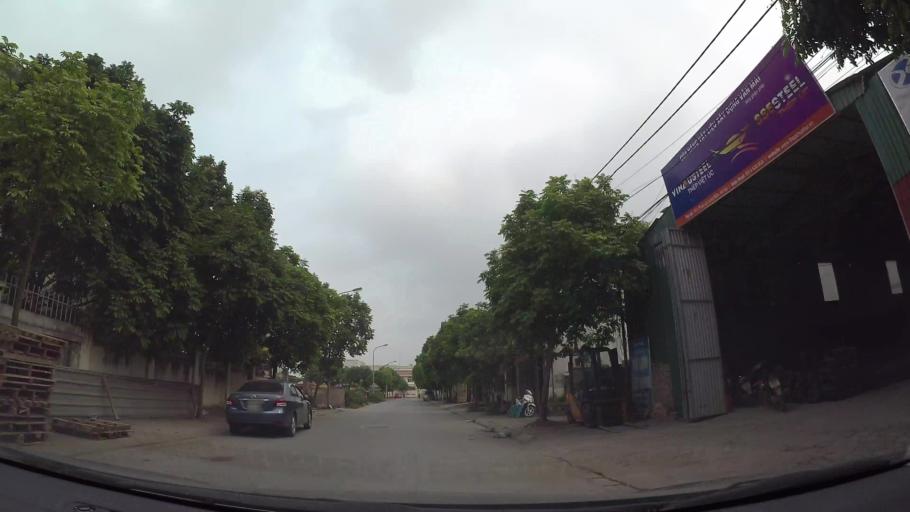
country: VN
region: Ha Noi
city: Trau Quy
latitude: 21.0451
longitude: 105.9254
